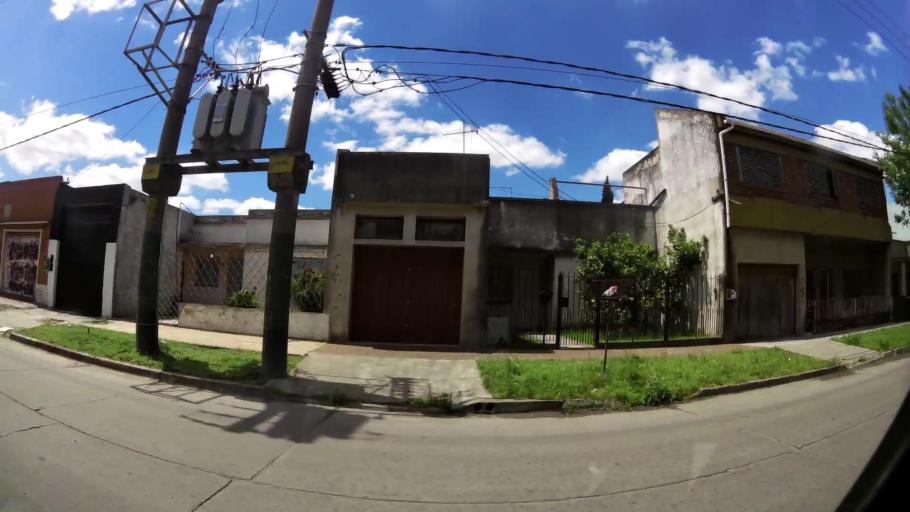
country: AR
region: Buenos Aires
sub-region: Partido de Lomas de Zamora
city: Lomas de Zamora
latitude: -34.7303
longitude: -58.4218
